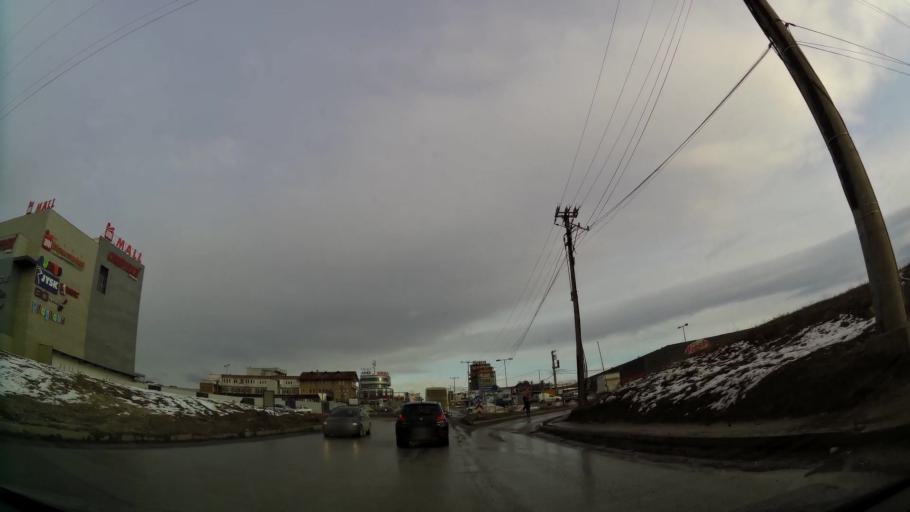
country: XK
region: Pristina
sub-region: Komuna e Prishtines
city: Pristina
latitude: 42.6309
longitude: 21.1507
